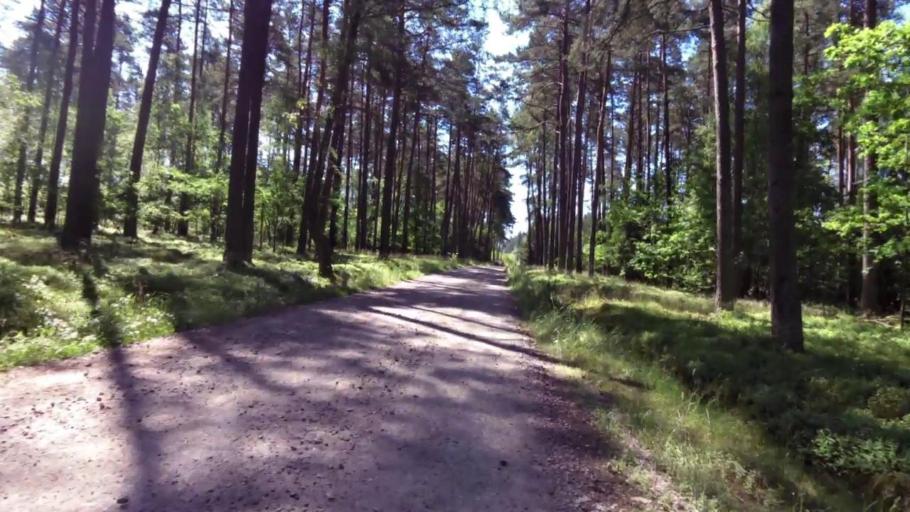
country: PL
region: West Pomeranian Voivodeship
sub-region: Powiat swidwinski
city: Rabino
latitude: 53.9059
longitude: 16.0072
